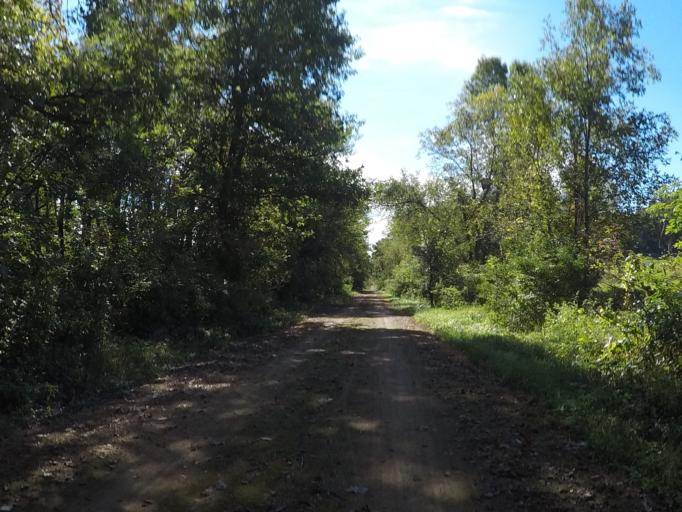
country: US
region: Wisconsin
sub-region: Richland County
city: Richland Center
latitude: 43.2823
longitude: -90.3184
